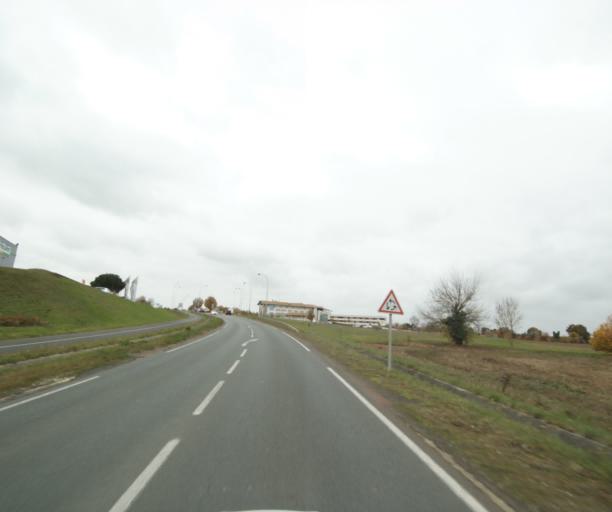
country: FR
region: Poitou-Charentes
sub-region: Departement de la Charente-Maritime
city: Saintes
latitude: 45.7572
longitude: -0.6507
